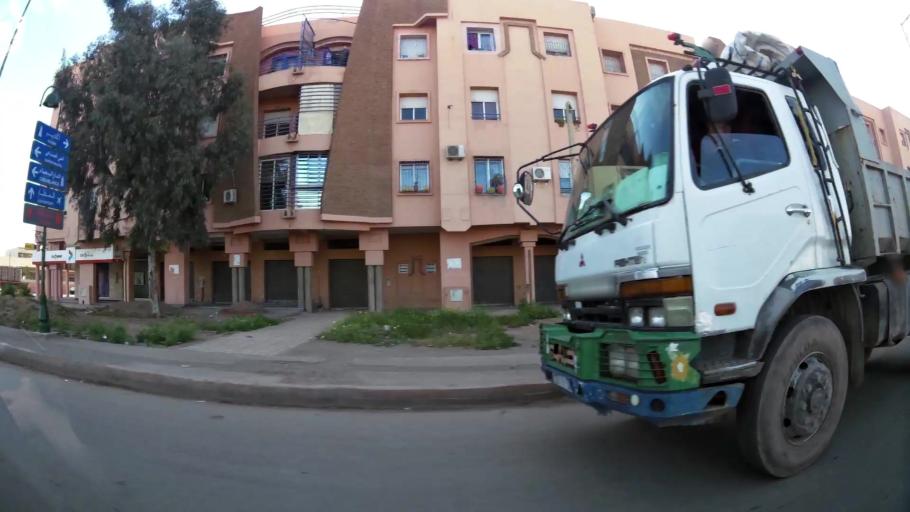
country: MA
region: Marrakech-Tensift-Al Haouz
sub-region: Marrakech
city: Marrakesh
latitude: 31.6831
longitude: -8.0613
